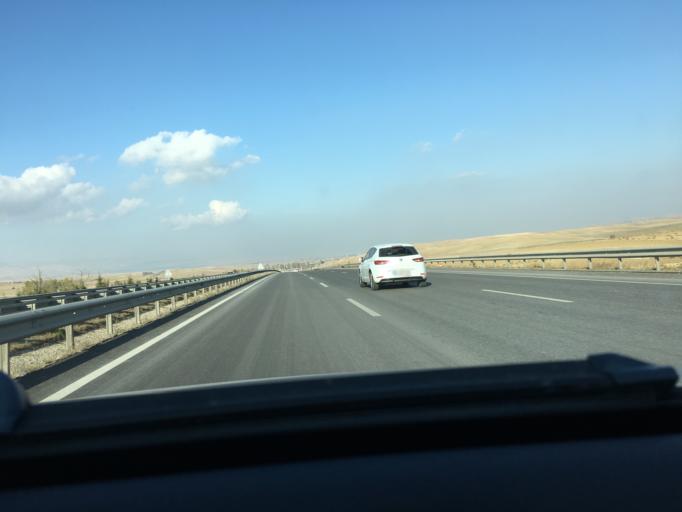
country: TR
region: Ankara
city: Polatli
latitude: 39.6166
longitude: 32.1876
